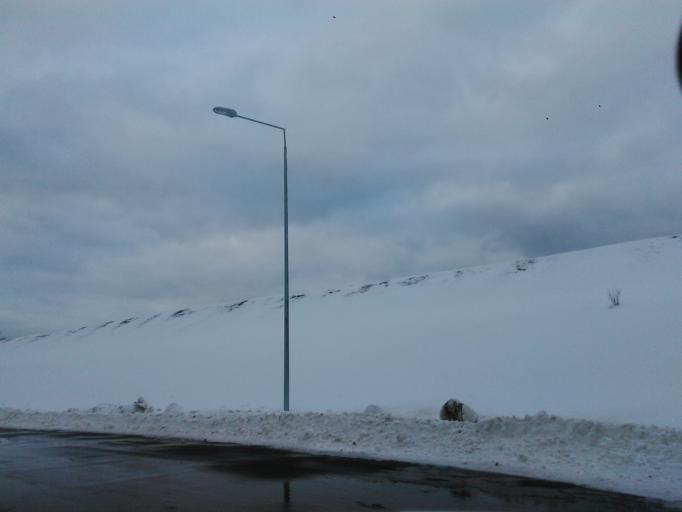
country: RU
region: Moskovskaya
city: Rzhavki
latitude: 56.0006
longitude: 37.2610
